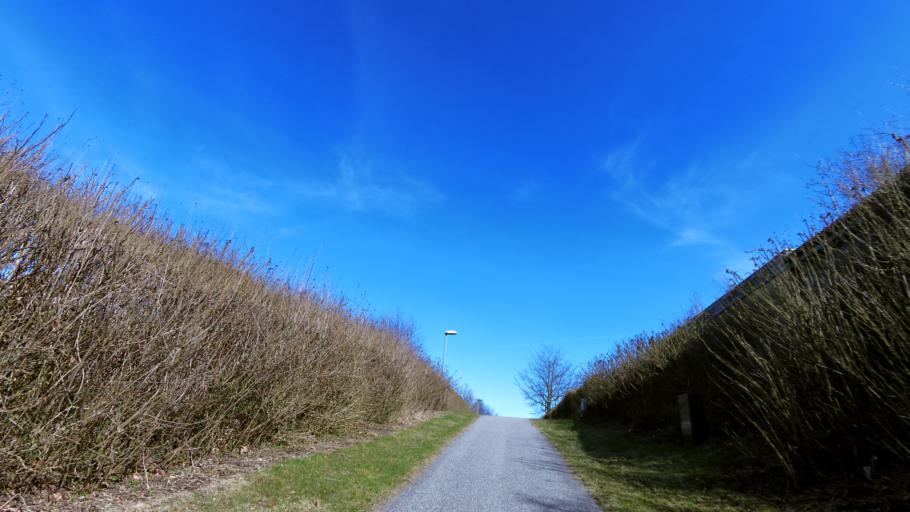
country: DK
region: Central Jutland
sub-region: Arhus Kommune
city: Stavtrup
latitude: 56.1792
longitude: 10.1009
